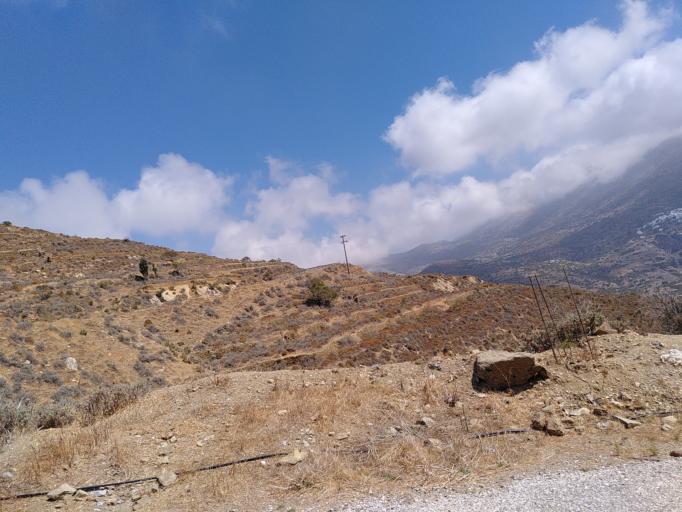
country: GR
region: South Aegean
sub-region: Nomos Kykladon
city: Amorgos
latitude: 36.9125
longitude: 25.9772
